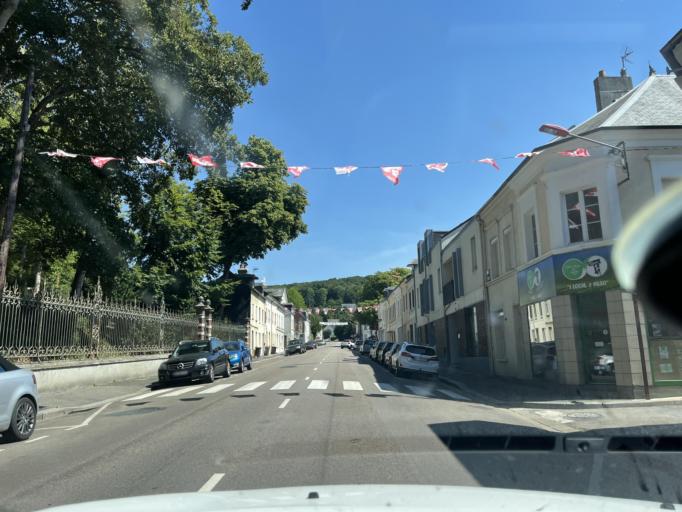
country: FR
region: Haute-Normandie
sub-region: Departement de la Seine-Maritime
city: Lillebonne
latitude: 49.5180
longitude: 0.5387
